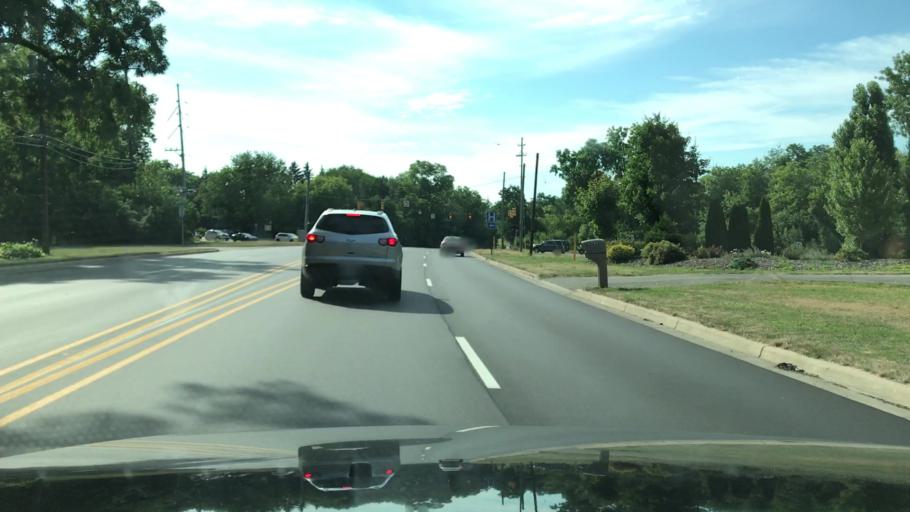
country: US
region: Michigan
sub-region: Kent County
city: East Grand Rapids
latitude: 42.9605
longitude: -85.6041
